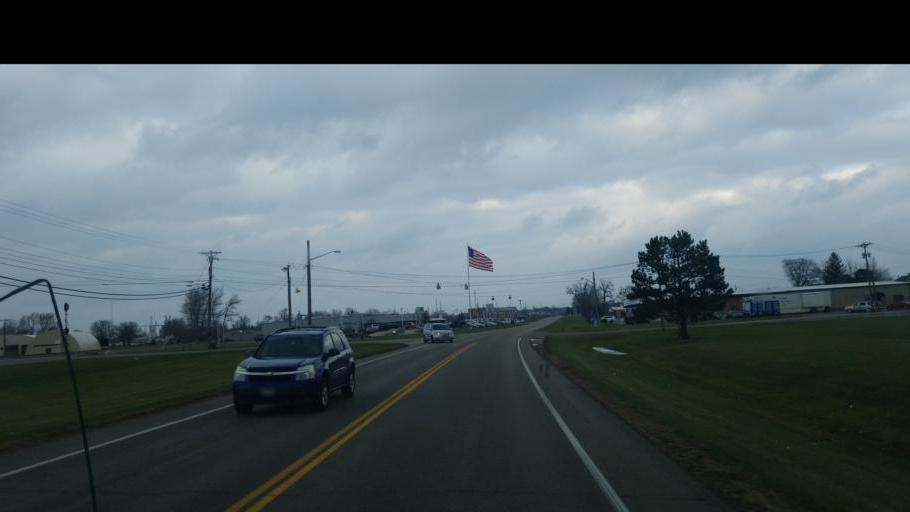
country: US
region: Ohio
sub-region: Mercer County
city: Celina
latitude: 40.5377
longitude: -84.5759
